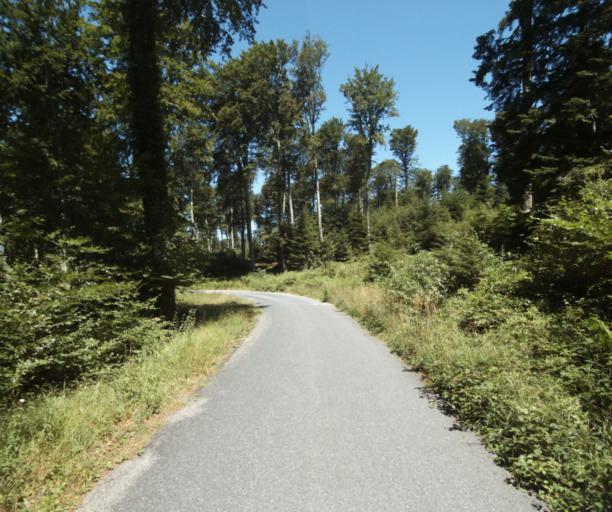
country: FR
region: Midi-Pyrenees
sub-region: Departement du Tarn
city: Dourgne
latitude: 43.4114
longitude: 2.1888
